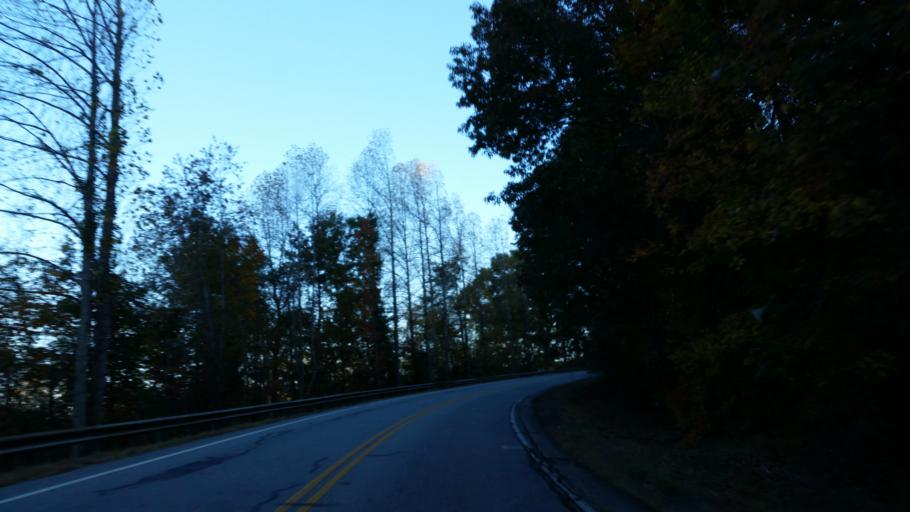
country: US
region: Georgia
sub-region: Lumpkin County
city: Dahlonega
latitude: 34.5354
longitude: -84.0599
